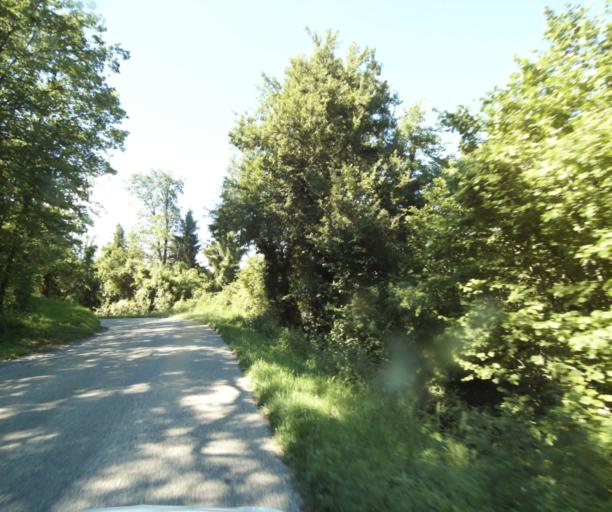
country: FR
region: Rhone-Alpes
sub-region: Departement de la Haute-Savoie
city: Sciez
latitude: 46.3178
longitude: 6.3858
